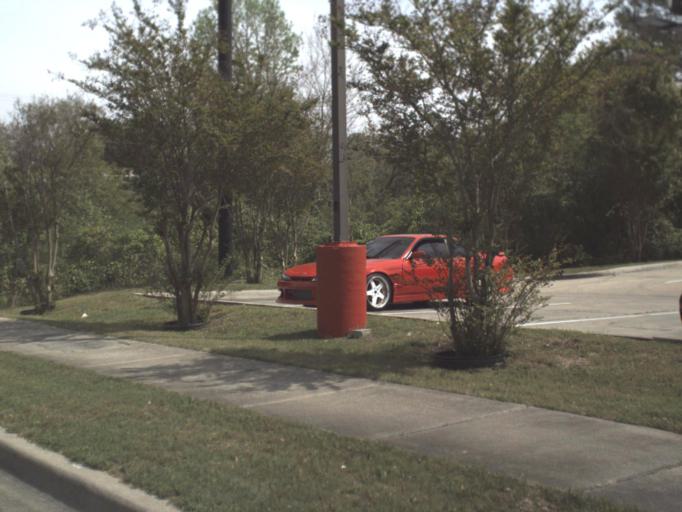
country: US
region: Florida
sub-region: Okaloosa County
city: Niceville
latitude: 30.5210
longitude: -86.4889
